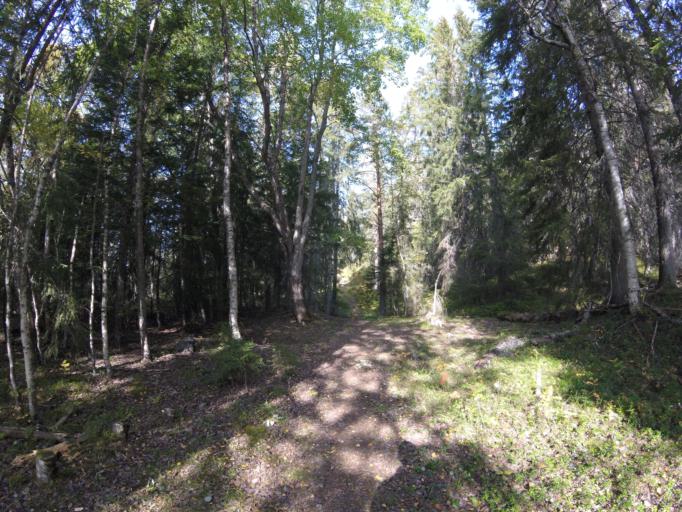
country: NO
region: Buskerud
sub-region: Kongsberg
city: Kongsberg
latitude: 59.6537
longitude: 9.5107
